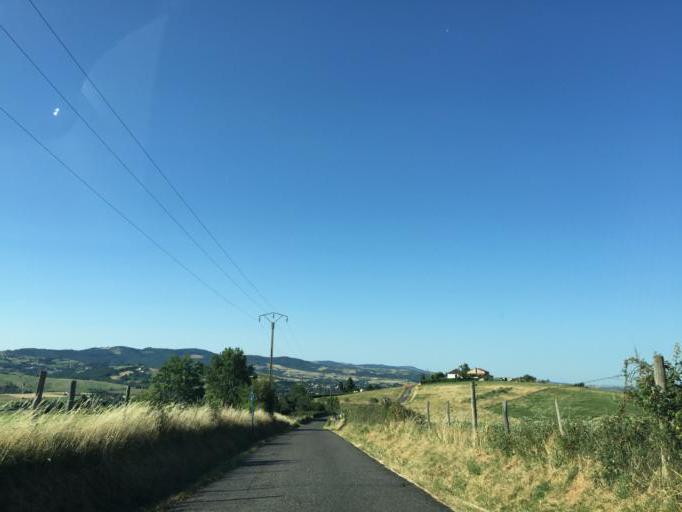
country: FR
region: Rhone-Alpes
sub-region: Departement de la Loire
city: Saint-Jean-Bonnefonds
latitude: 45.4524
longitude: 4.4908
